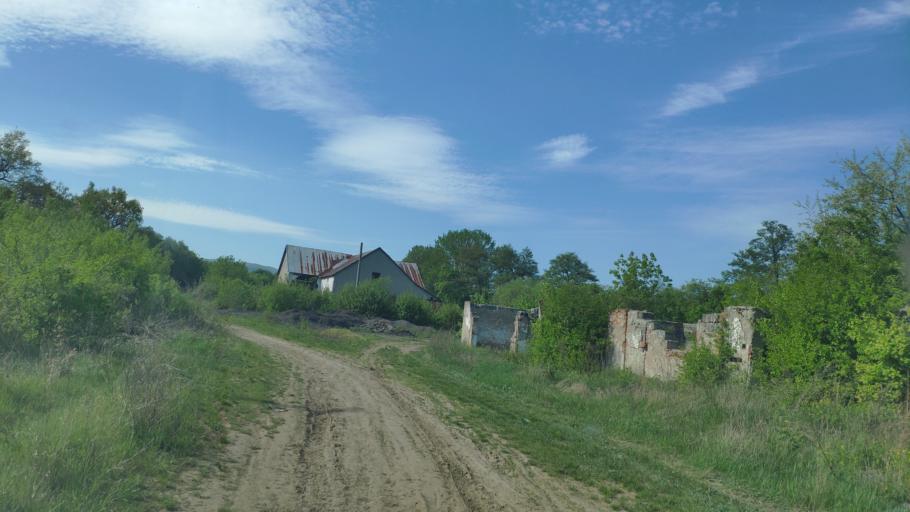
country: SK
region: Kosicky
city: Secovce
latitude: 48.7090
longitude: 21.6143
